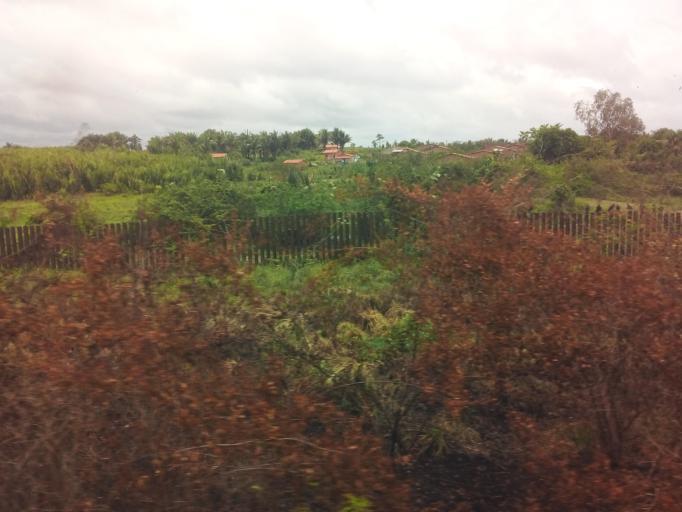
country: BR
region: Maranhao
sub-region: Vitoria Do Mearim
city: Vitoria do Mearim
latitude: -3.5869
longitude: -44.9666
